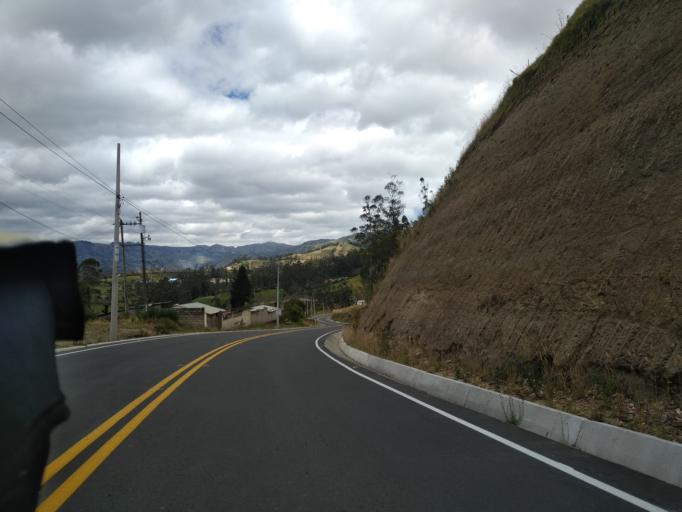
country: EC
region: Cotopaxi
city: Saquisili
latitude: -0.7121
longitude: -78.8835
